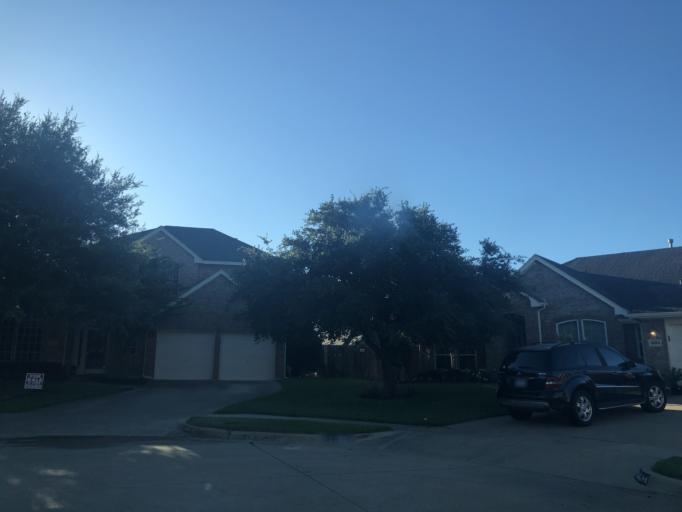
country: US
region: Texas
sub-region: Dallas County
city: Grand Prairie
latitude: 32.6627
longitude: -96.9983
